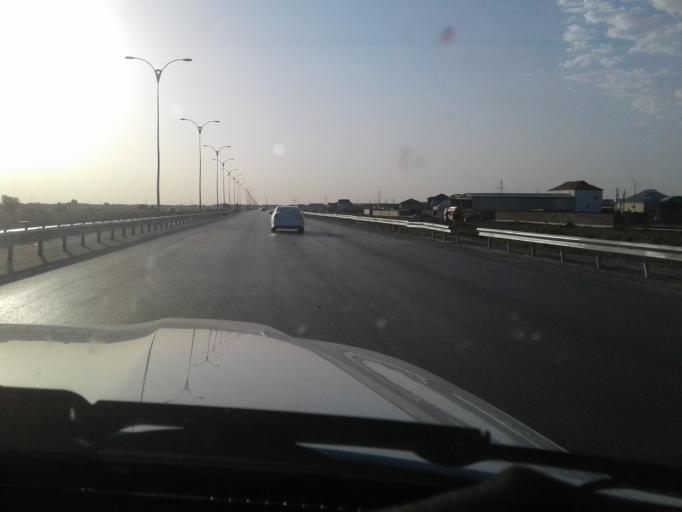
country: TM
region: Mary
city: Mary
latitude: 37.5596
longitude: 61.8505
